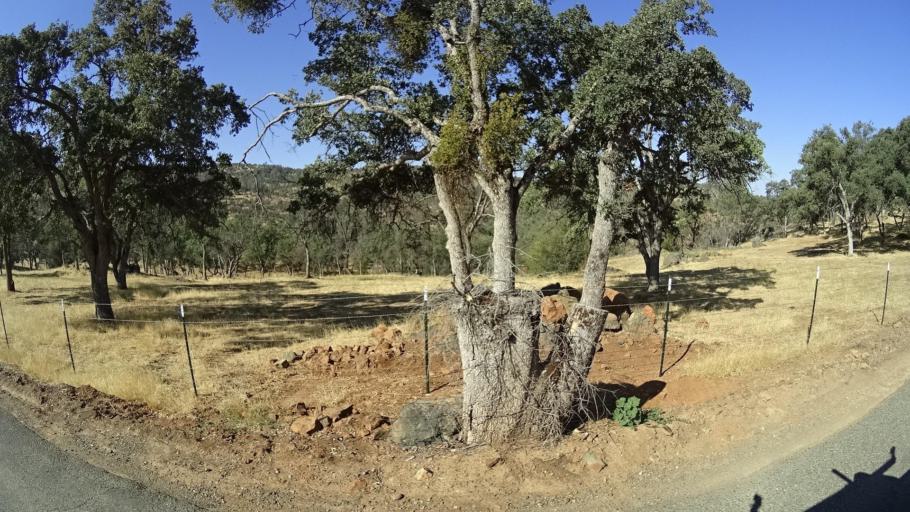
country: US
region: California
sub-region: Mariposa County
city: Mariposa
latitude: 37.5830
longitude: -120.1768
